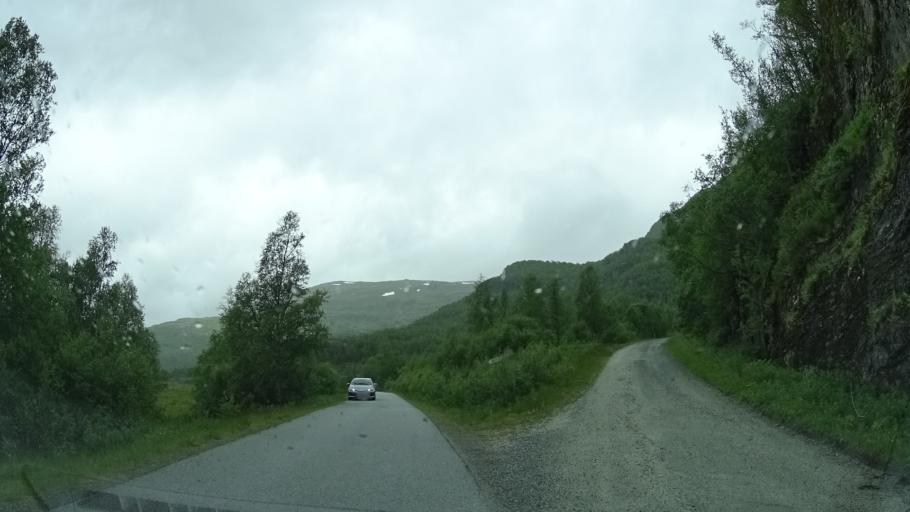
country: NO
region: Sogn og Fjordane
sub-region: Laerdal
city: Laerdalsoyri
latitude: 60.8263
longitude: 7.5192
